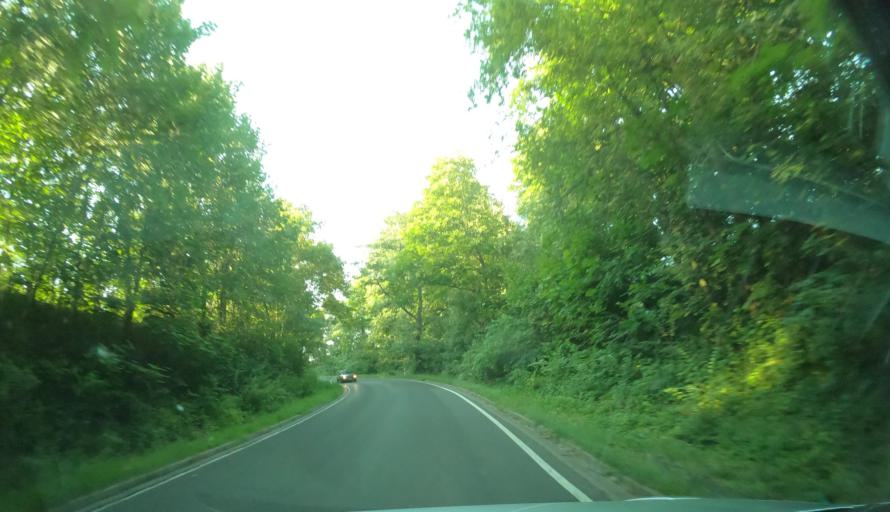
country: PL
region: Kujawsko-Pomorskie
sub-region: Powiat swiecki
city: Pruszcz
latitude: 53.2371
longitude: 18.2199
